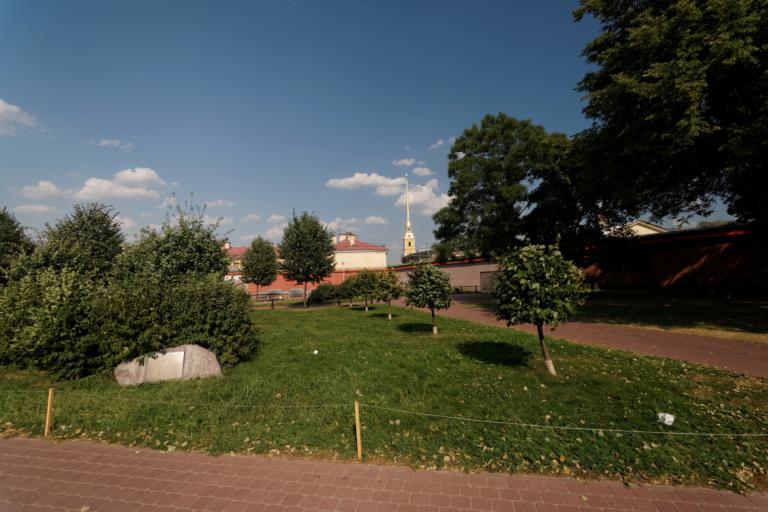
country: RU
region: St.-Petersburg
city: Saint Petersburg
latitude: 59.9491
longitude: 30.3100
